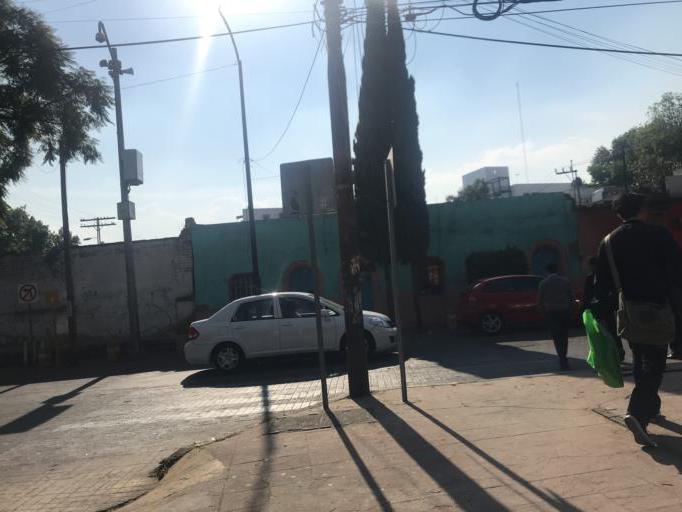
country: MX
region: Mexico City
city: Cuauhtemoc
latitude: 19.4530
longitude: -99.1742
